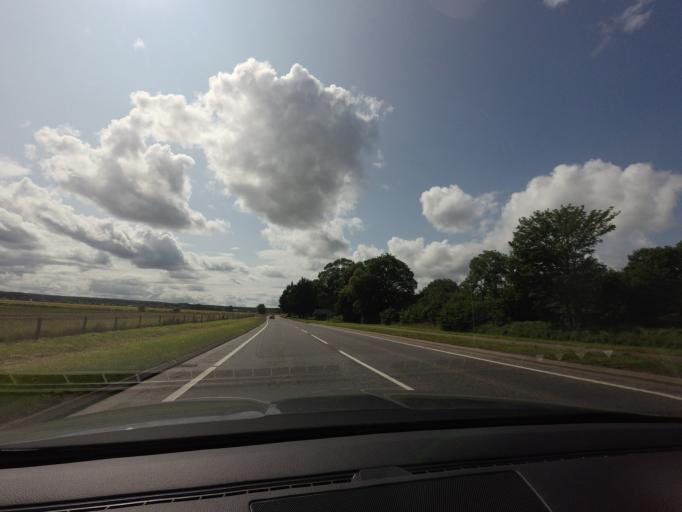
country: GB
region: Scotland
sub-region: Moray
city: Forres
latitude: 57.6048
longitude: -3.6417
